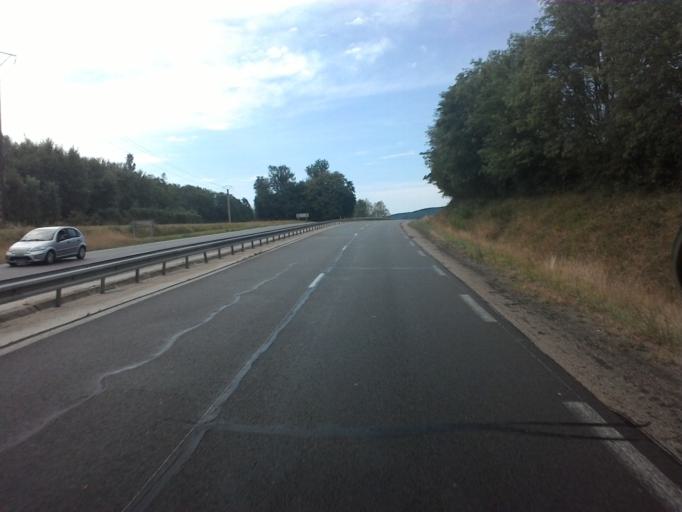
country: FR
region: Franche-Comte
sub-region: Departement du Jura
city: Montmorot
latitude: 46.7517
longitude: 5.5580
